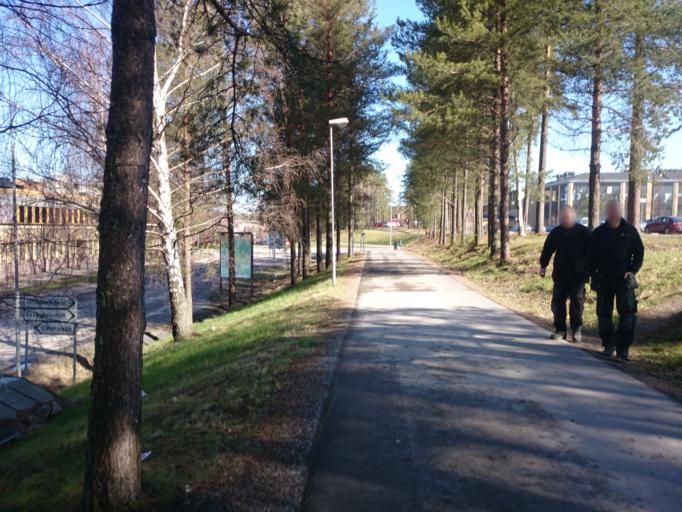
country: SE
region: Vaesterbotten
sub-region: Umea Kommun
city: Umea
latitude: 63.8171
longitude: 20.3045
